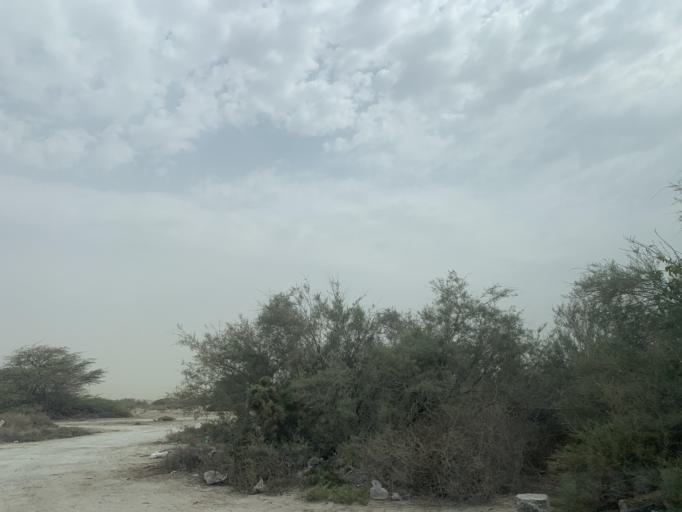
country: BH
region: Northern
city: Madinat `Isa
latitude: 26.1739
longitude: 50.5029
